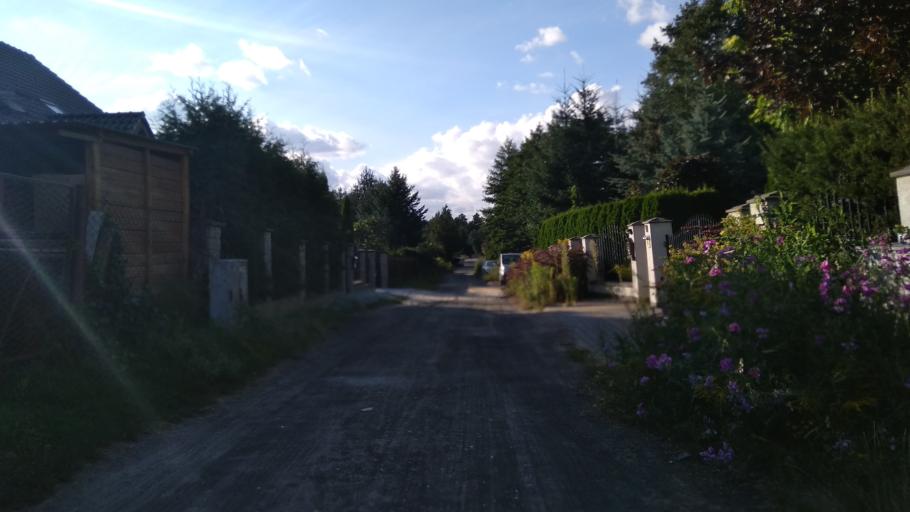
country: PL
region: Kujawsko-Pomorskie
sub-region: Powiat bydgoski
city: Osielsko
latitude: 53.2301
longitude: 18.1227
